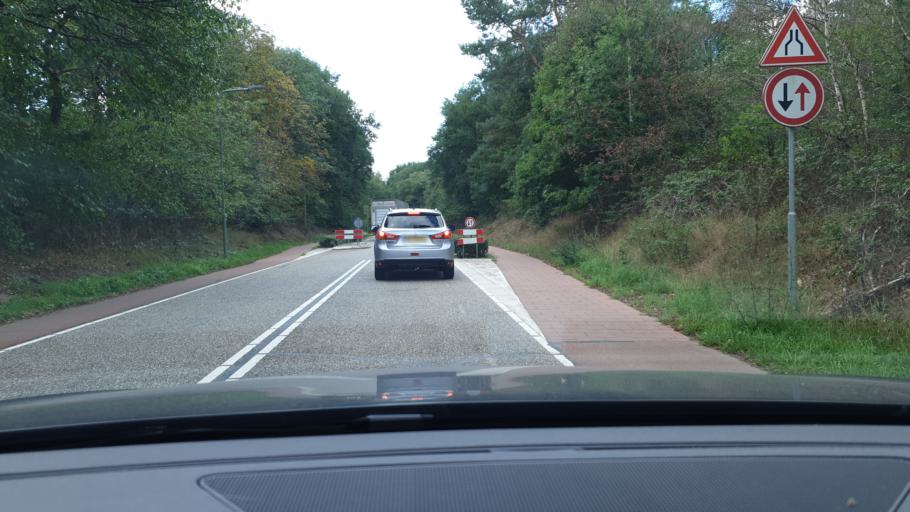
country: NL
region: North Brabant
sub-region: Gemeente Cuijk
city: Cuijk
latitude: 51.7610
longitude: 5.9006
